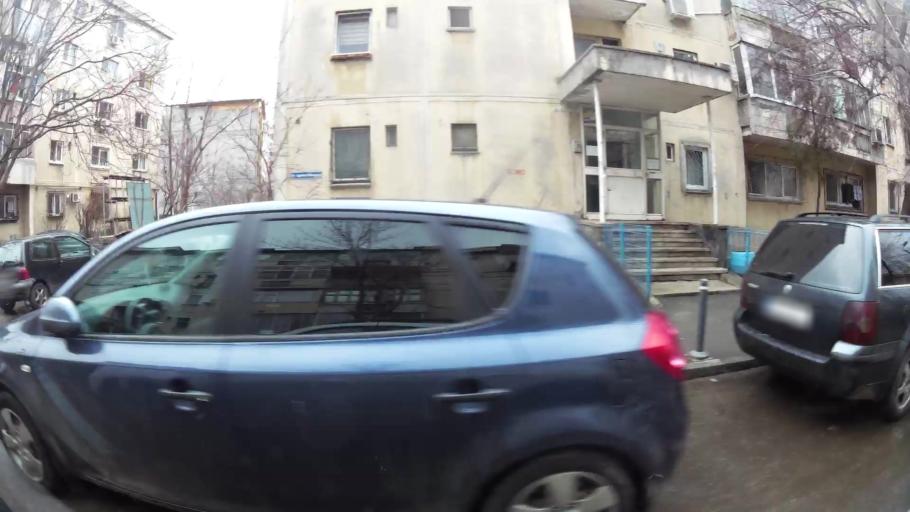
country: RO
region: Bucuresti
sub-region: Municipiul Bucuresti
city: Bucharest
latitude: 44.4187
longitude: 26.1326
